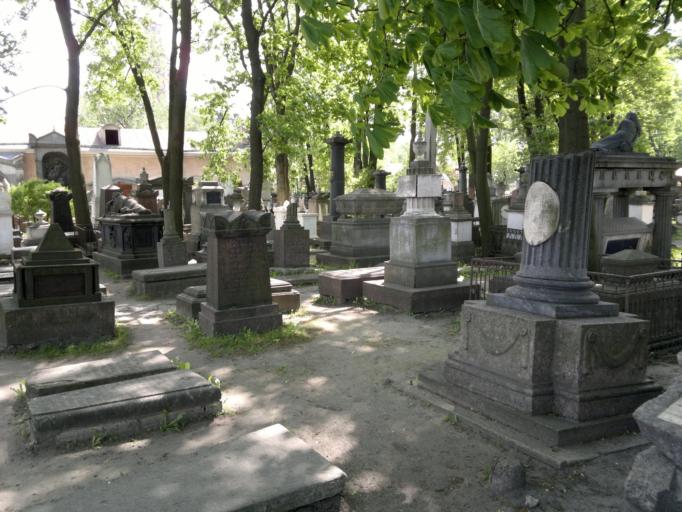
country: RU
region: St.-Petersburg
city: Centralniy
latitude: 59.9235
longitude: 30.3877
